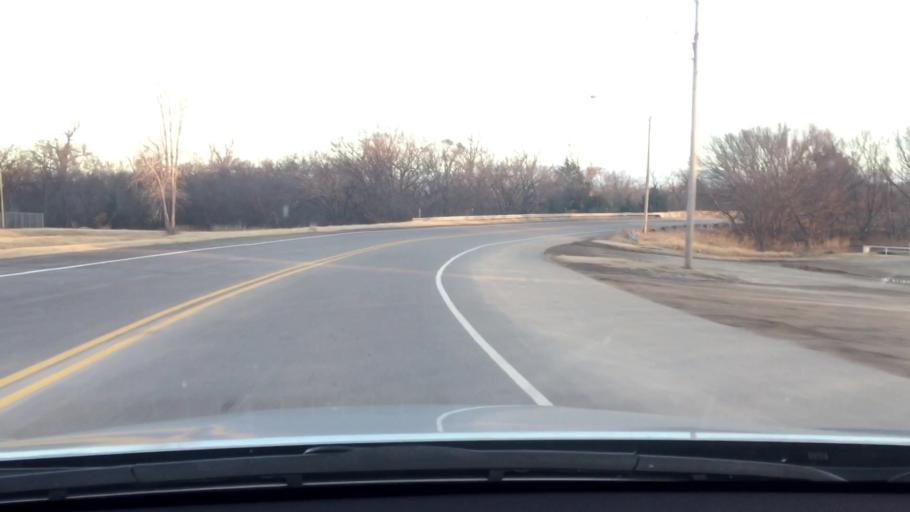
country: US
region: Oklahoma
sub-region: Carter County
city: Ardmore
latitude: 34.1735
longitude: -97.1764
